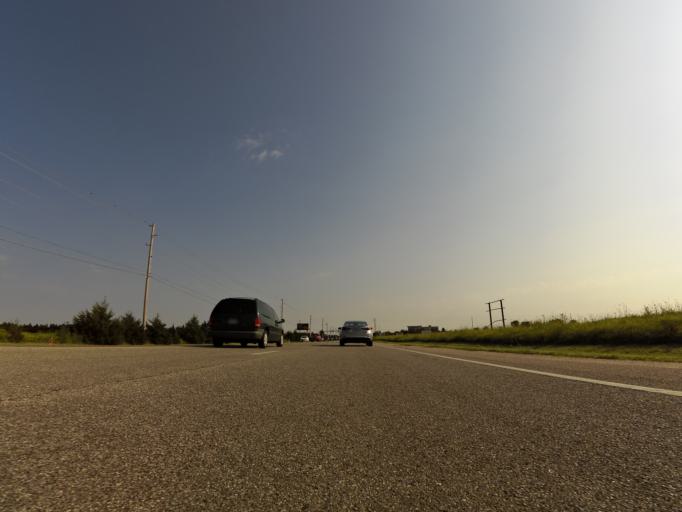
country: US
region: Kansas
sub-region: Sedgwick County
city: Maize
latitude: 37.7545
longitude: -97.4264
